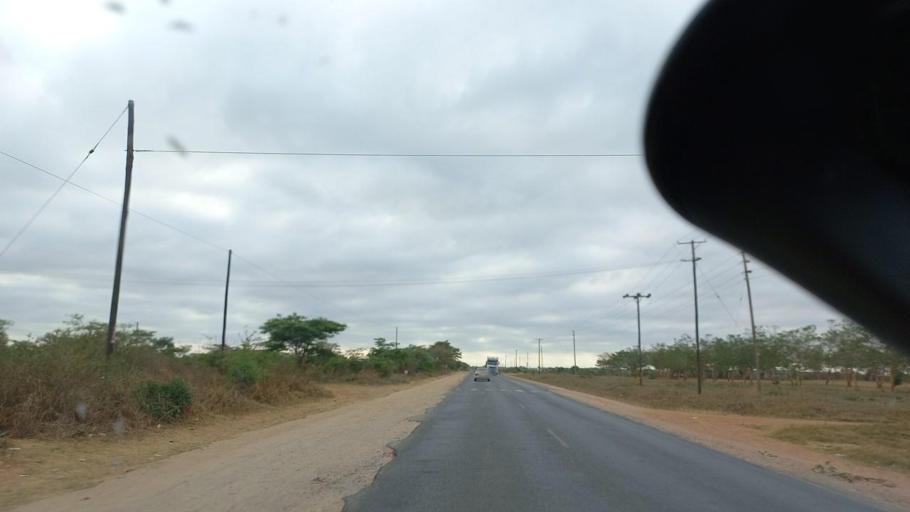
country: ZM
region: Lusaka
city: Chongwe
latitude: -15.3431
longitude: 28.6460
